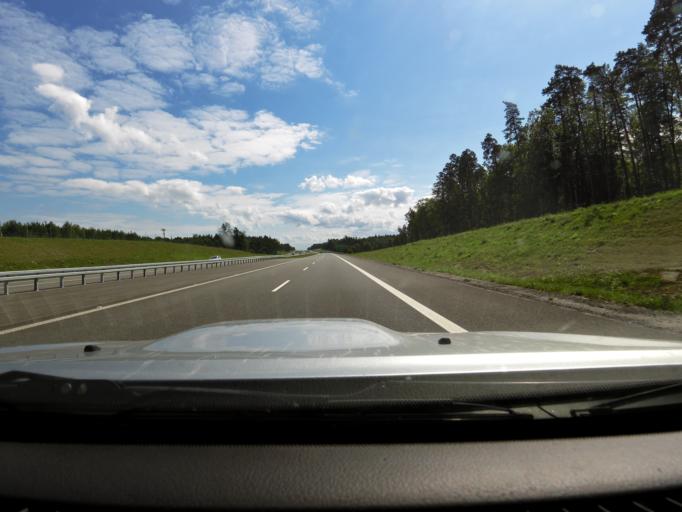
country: PL
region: Warmian-Masurian Voivodeship
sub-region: Powiat ostrodzki
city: Milomlyn
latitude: 53.7444
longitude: 19.8911
